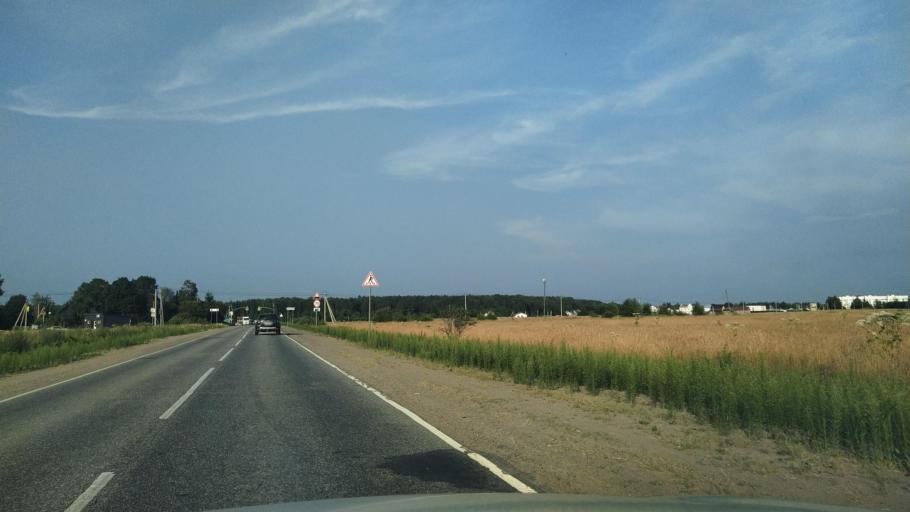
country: RU
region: Leningrad
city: Koltushi
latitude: 59.8894
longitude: 30.7291
